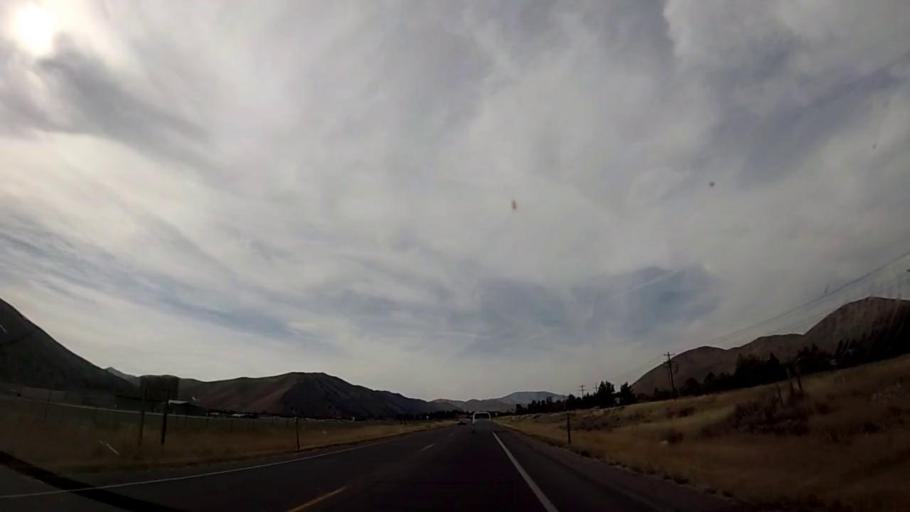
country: US
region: Idaho
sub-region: Blaine County
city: Hailey
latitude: 43.5079
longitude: -114.2978
